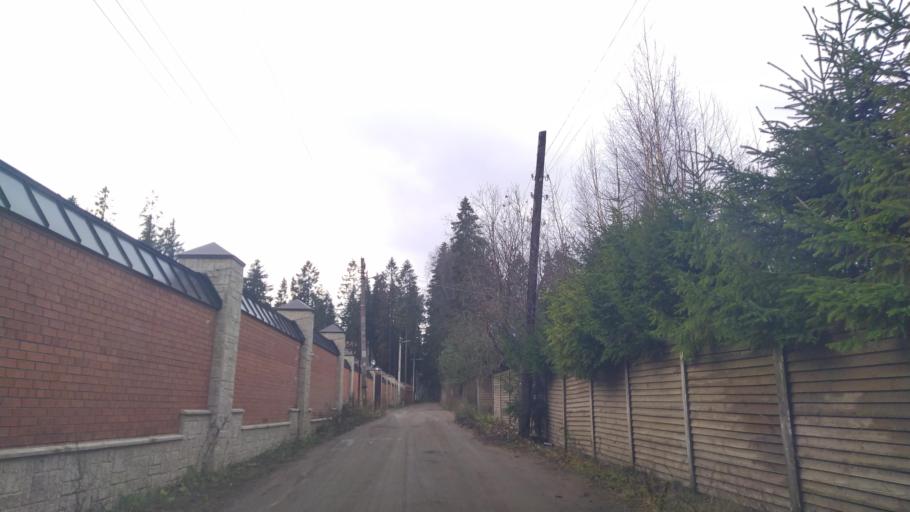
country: RU
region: Leningrad
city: Vsevolozhsk
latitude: 60.0233
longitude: 30.6744
